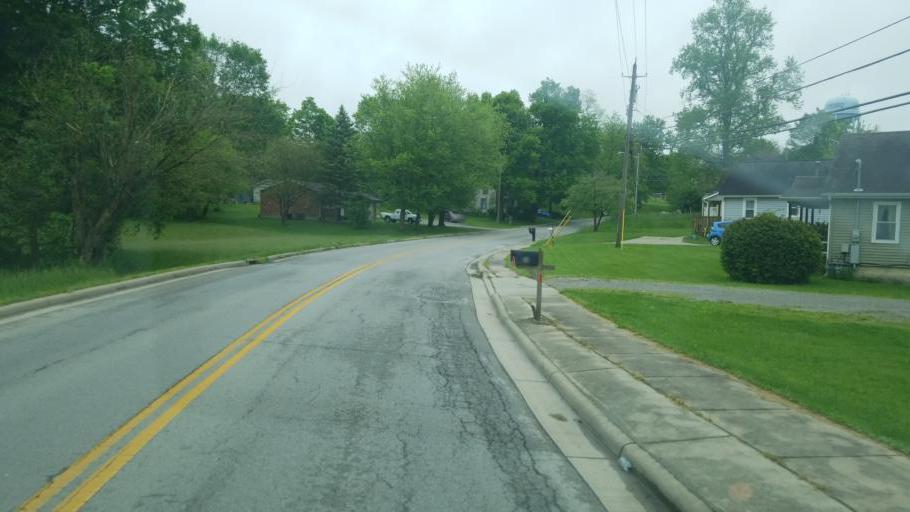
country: US
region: Ohio
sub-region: Highland County
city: Hillsboro
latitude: 39.2135
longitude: -83.6127
